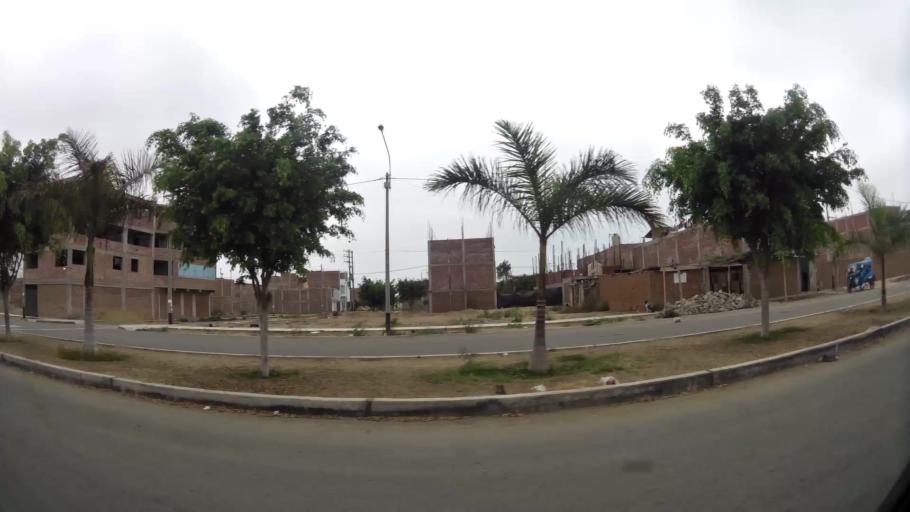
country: PE
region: La Libertad
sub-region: Provincia de Trujillo
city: La Esperanza
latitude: -8.0850
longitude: -79.0489
